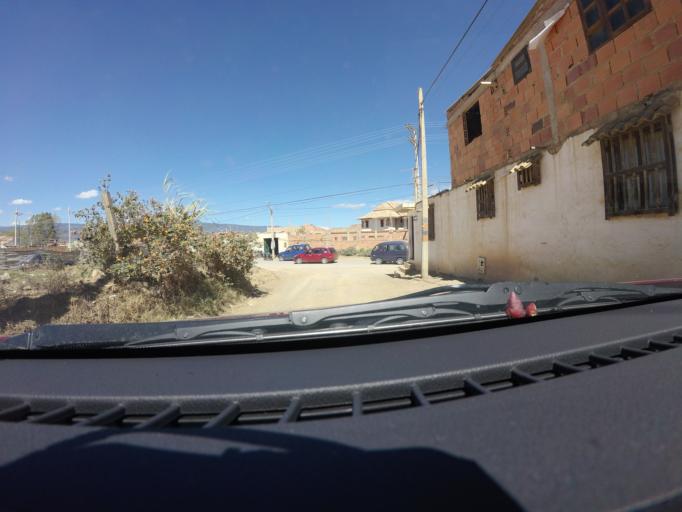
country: CO
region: Boyaca
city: Villa de Leiva
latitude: 5.6326
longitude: -73.5289
